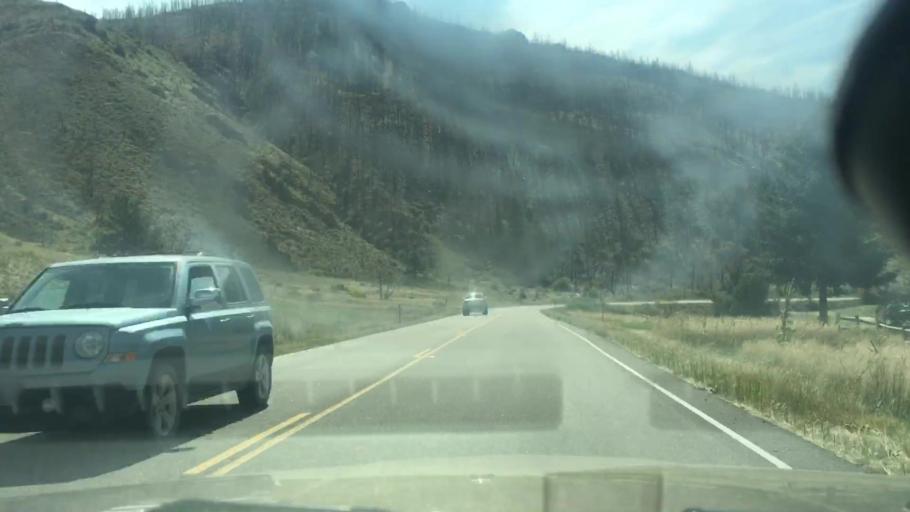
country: US
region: Colorado
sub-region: Larimer County
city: Laporte
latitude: 40.6908
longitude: -105.4319
